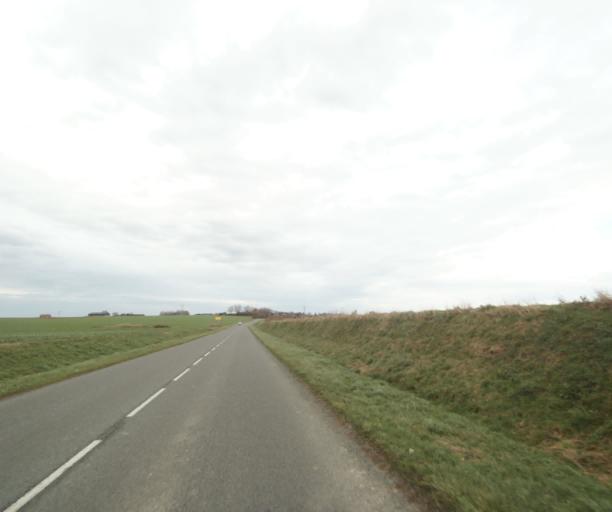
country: FR
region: Nord-Pas-de-Calais
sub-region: Departement du Nord
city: Sebourg
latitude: 50.3293
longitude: 3.6341
